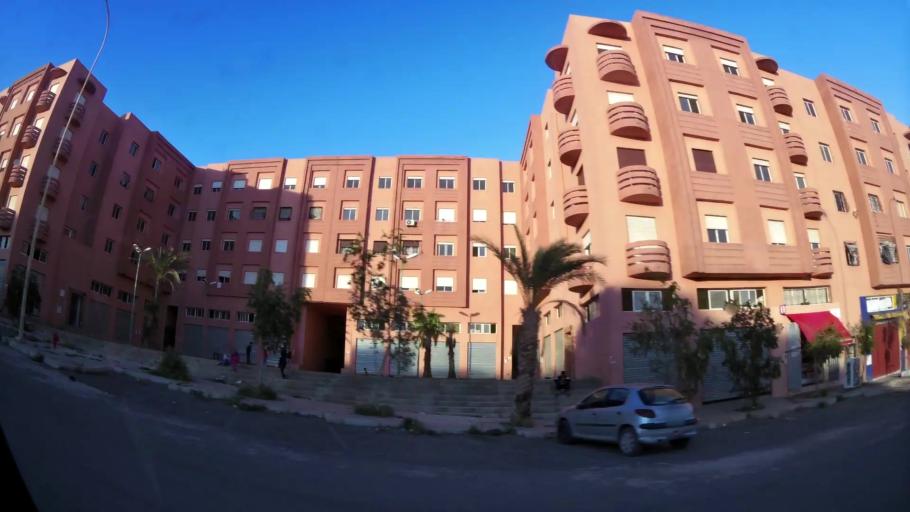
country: MA
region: Marrakech-Tensift-Al Haouz
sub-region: Marrakech
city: Marrakesh
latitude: 31.7520
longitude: -8.1224
